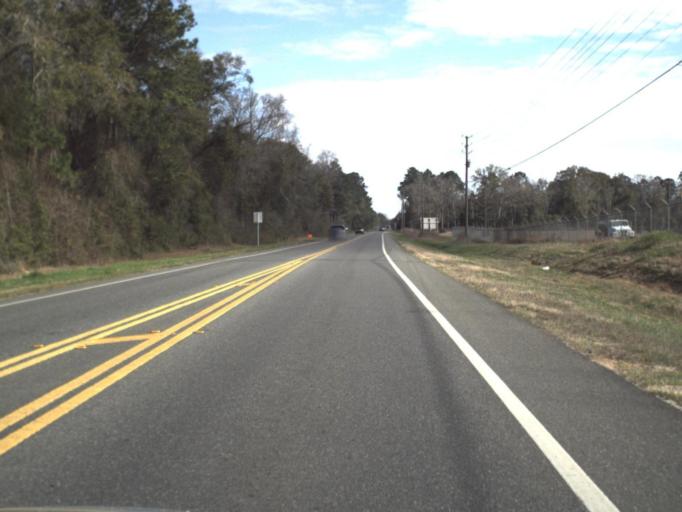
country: US
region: Florida
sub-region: Jackson County
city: Marianna
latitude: 30.8141
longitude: -85.1740
